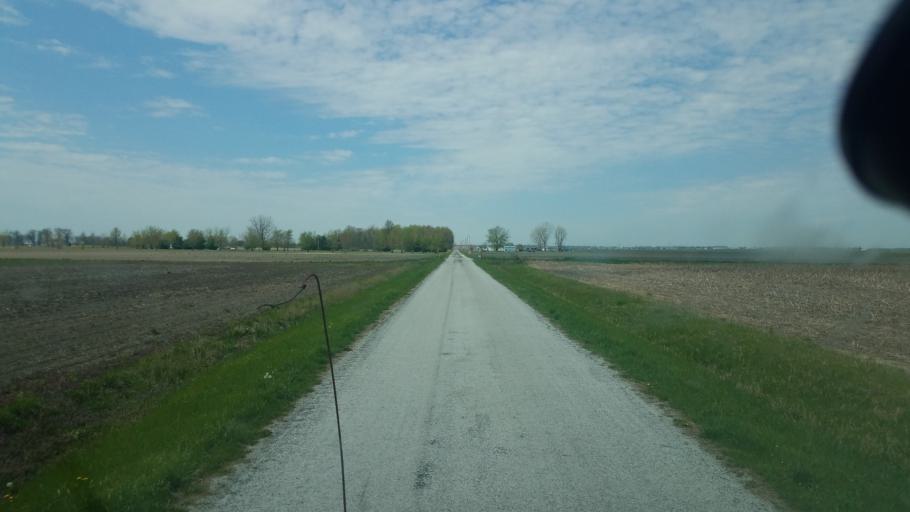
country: US
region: Ohio
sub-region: Hardin County
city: Ada
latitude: 40.6566
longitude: -83.7572
